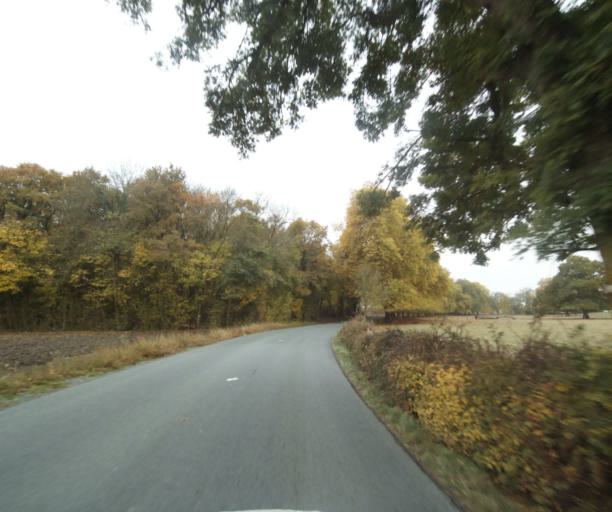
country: FR
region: Poitou-Charentes
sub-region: Departement de la Charente-Maritime
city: Chermignac
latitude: 45.7183
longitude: -0.6750
